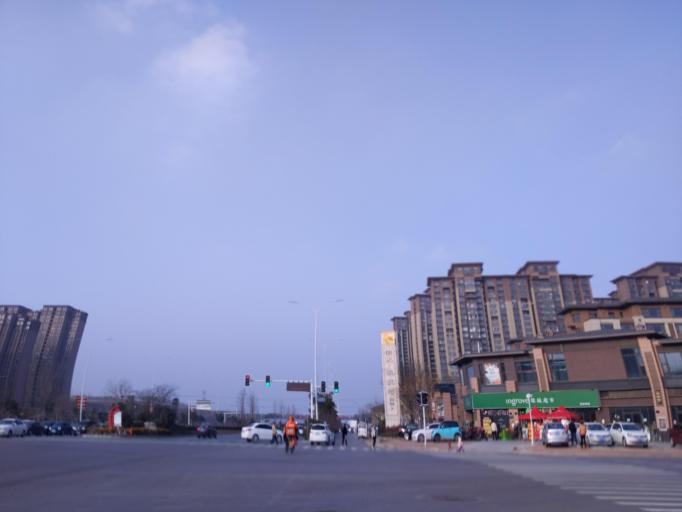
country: CN
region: Henan Sheng
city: Puyang
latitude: 35.8134
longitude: 115.0225
